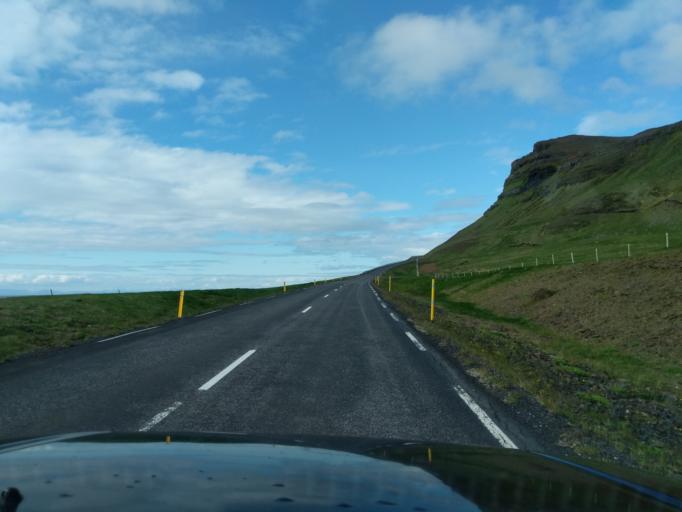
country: IS
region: West
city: Olafsvik
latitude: 64.9350
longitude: -23.5048
